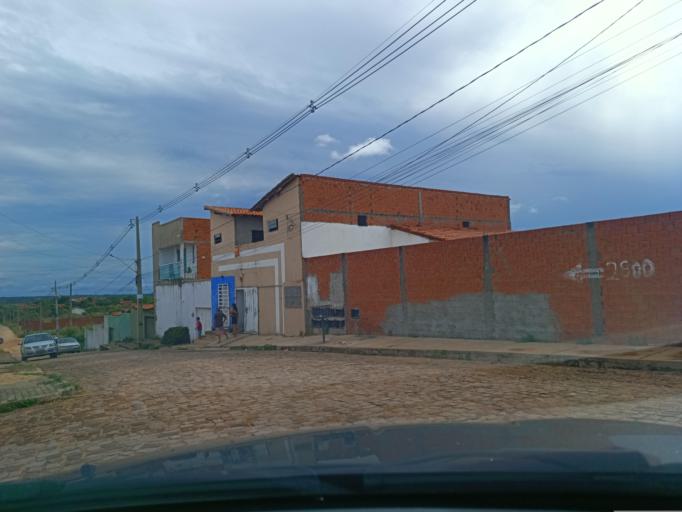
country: BR
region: Piaui
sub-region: Teresina
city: Teresina
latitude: -5.1627
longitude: -42.7774
